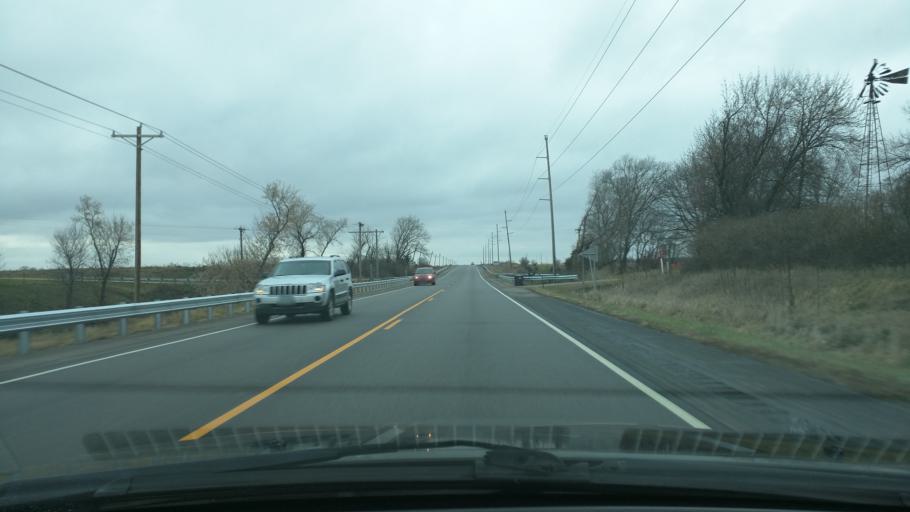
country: US
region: Minnesota
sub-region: Dakota County
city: Hastings
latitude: 44.7385
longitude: -92.9274
